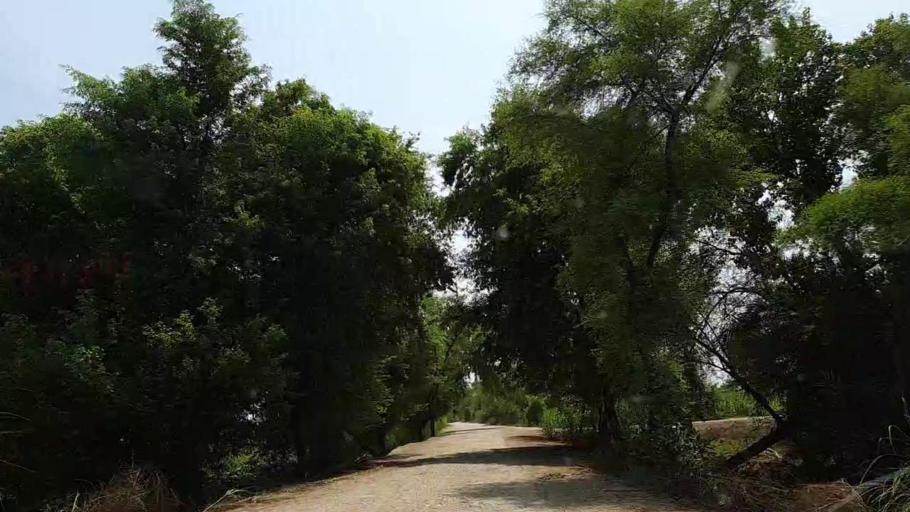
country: PK
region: Sindh
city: Adilpur
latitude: 27.9275
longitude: 69.3795
